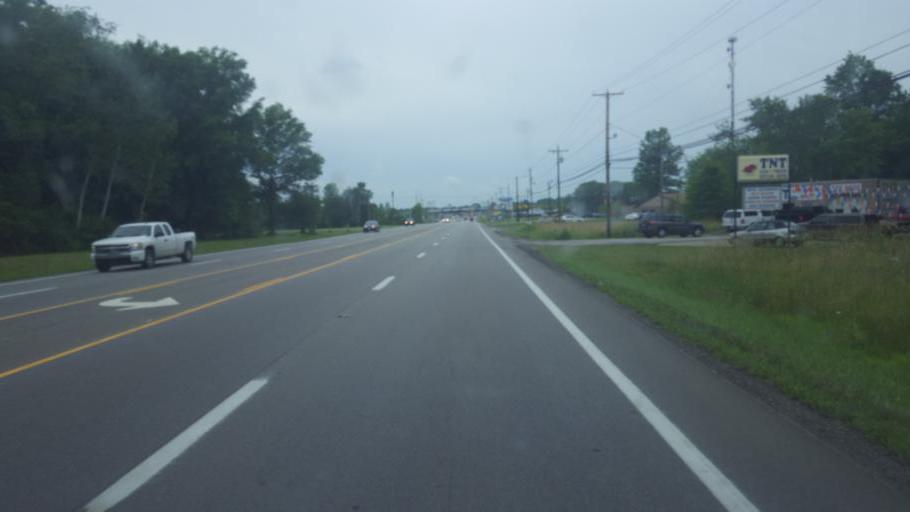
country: US
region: Ohio
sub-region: Trumbull County
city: Morgandale
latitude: 41.2800
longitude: -80.7725
